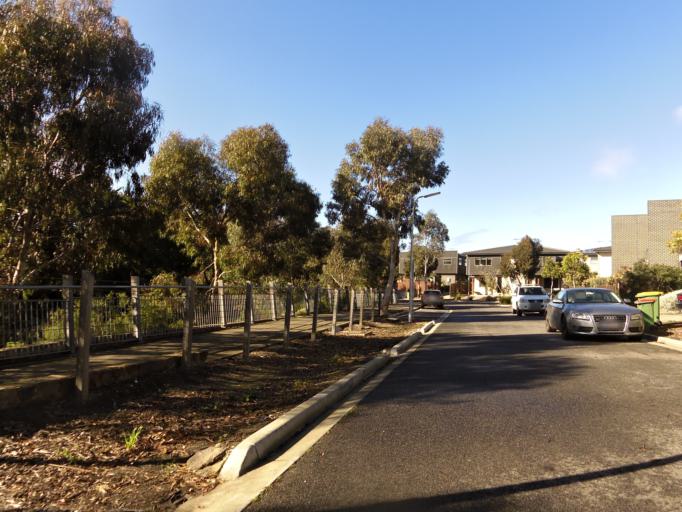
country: AU
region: Victoria
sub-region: Maribyrnong
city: Kingsville
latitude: -37.8081
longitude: 144.8664
